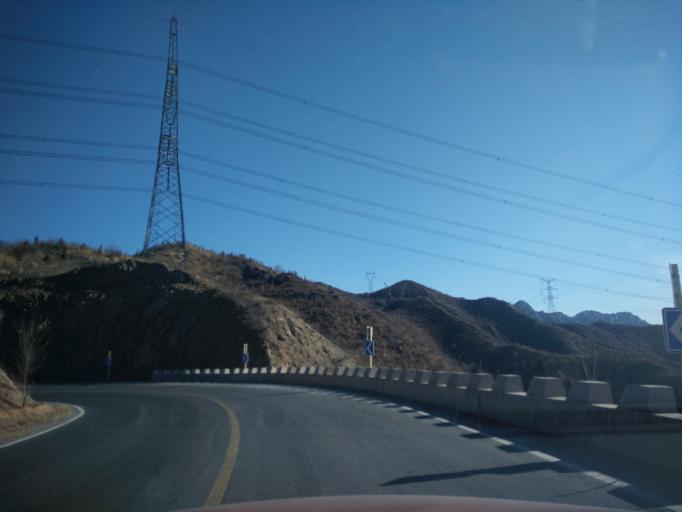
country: CN
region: Beijing
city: Zhaitang
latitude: 40.0302
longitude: 115.7101
